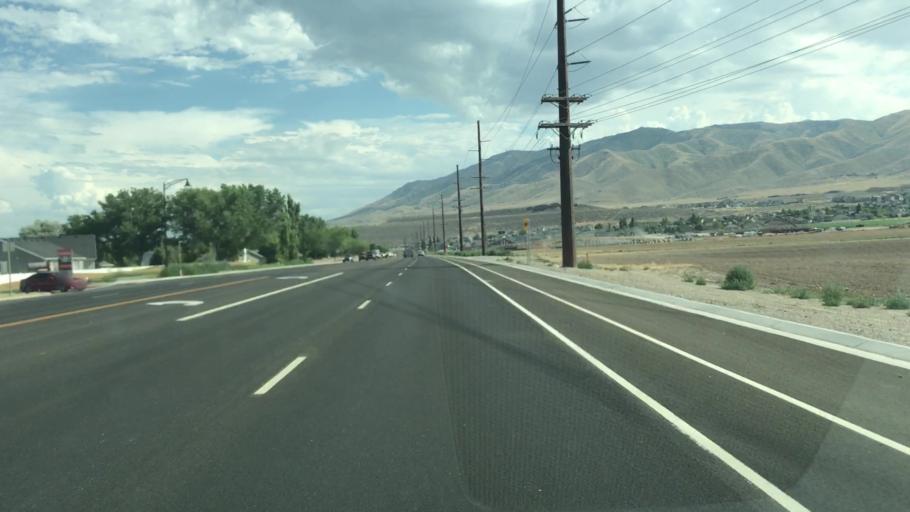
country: US
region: Utah
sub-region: Utah County
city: Saratoga Springs
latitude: 40.3487
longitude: -111.9165
